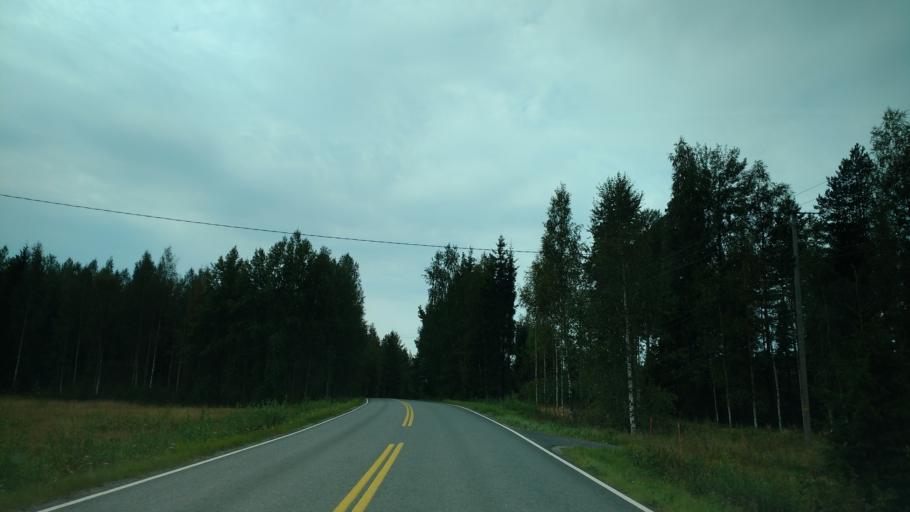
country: FI
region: Varsinais-Suomi
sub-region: Salo
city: Kuusjoki
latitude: 60.5015
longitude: 23.1681
